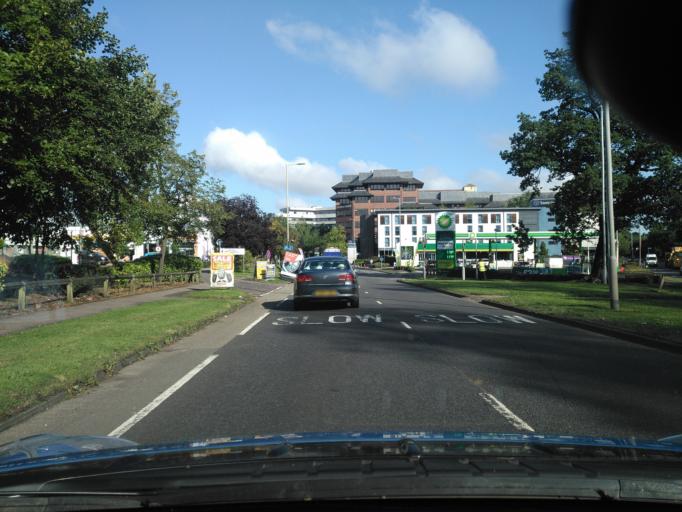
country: GB
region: England
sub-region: Hertfordshire
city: Borehamwood
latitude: 51.6578
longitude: -0.2521
